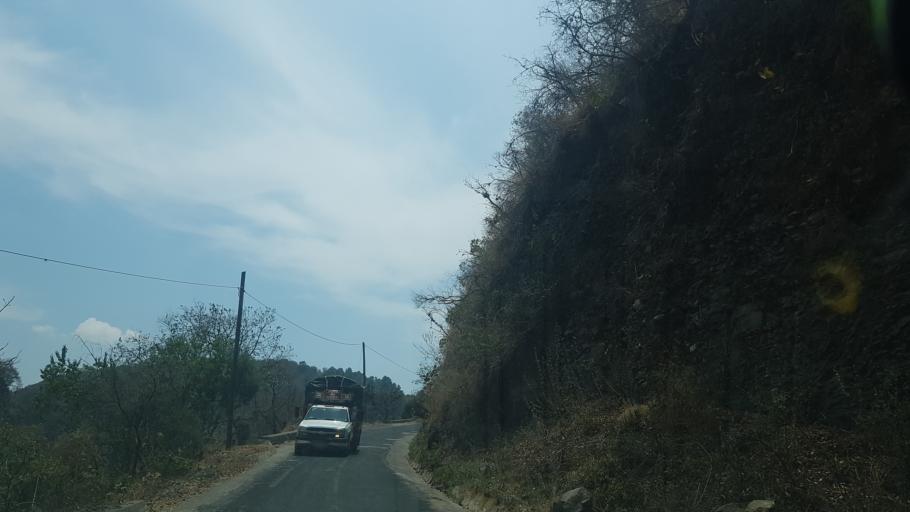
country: MX
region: Puebla
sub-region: Tochimilco
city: La Magdalena Yancuitlalpan
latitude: 18.8742
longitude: -98.6112
